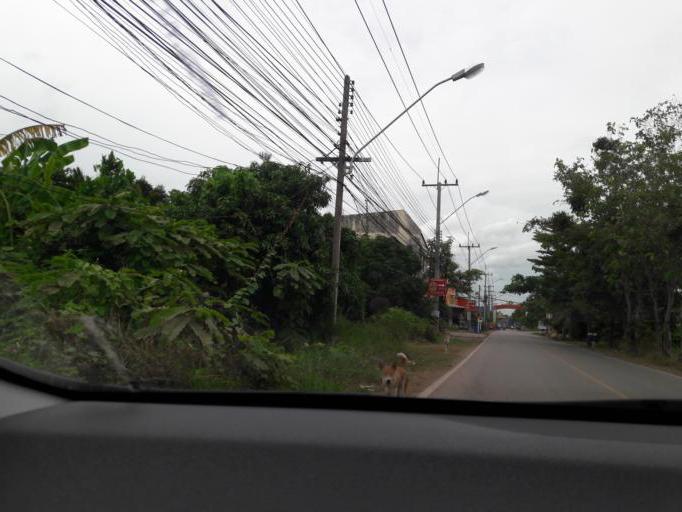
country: TH
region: Samut Sakhon
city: Ban Phaeo
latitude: 13.5541
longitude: 100.0436
